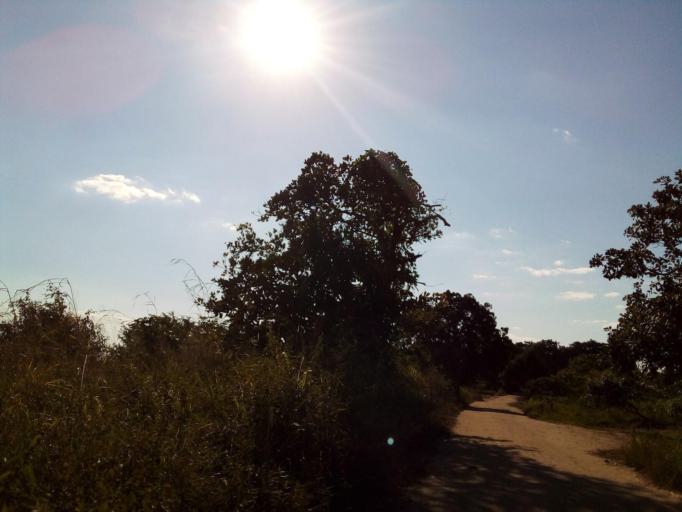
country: MZ
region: Zambezia
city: Quelimane
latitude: -17.5356
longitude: 36.6871
